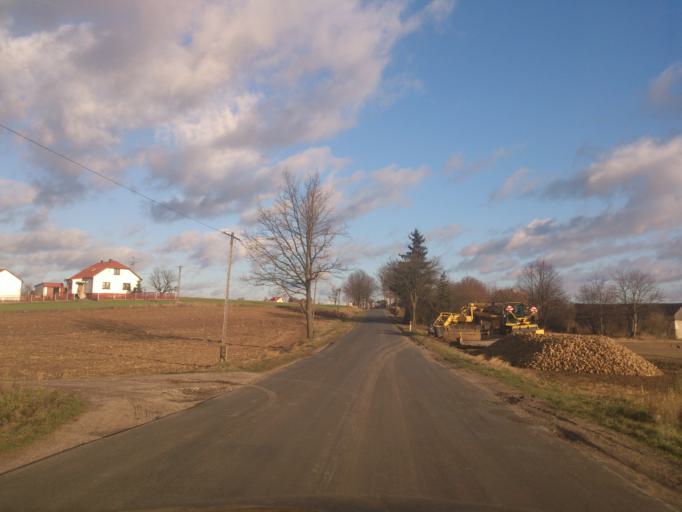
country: PL
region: Kujawsko-Pomorskie
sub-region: Powiat golubsko-dobrzynski
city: Ciechocin
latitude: 53.0493
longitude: 18.9079
